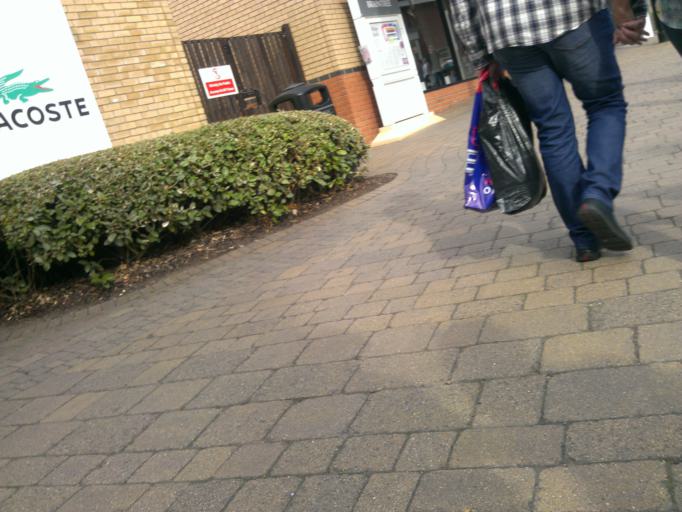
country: GB
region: England
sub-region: Essex
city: Rayne
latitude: 51.8696
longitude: 0.5702
